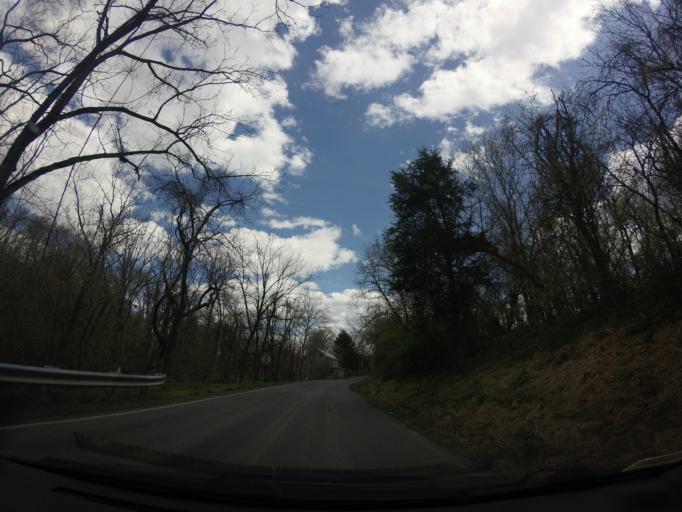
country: US
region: Maryland
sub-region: Washington County
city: Keedysville
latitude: 39.4666
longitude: -77.7195
